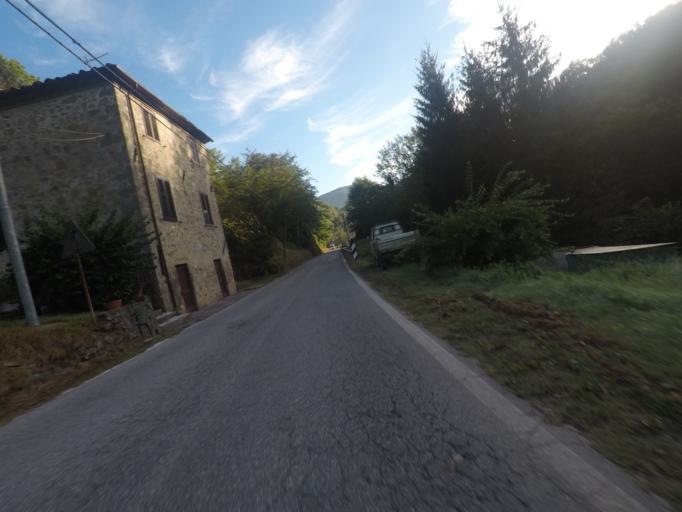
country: IT
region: Tuscany
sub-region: Provincia di Lucca
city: Valdottavo
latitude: 43.9589
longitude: 10.4548
